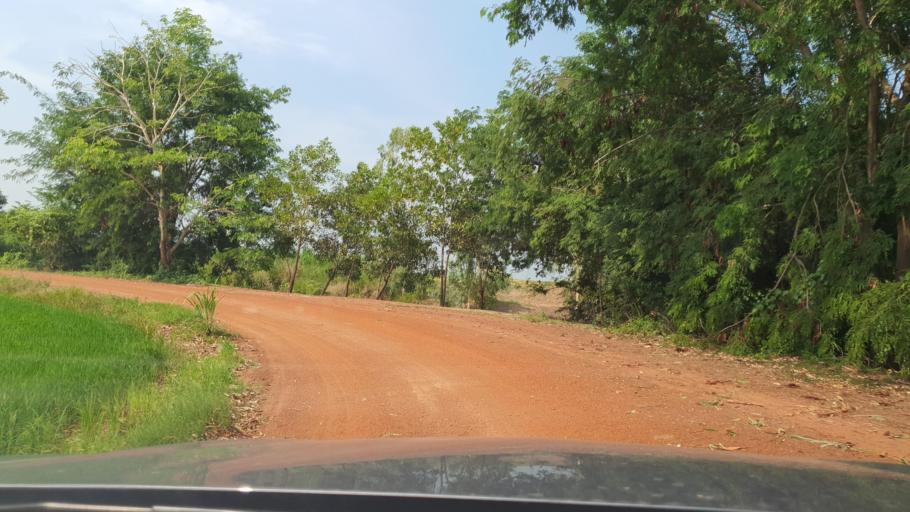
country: TH
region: Phitsanulok
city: Bang Rakam
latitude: 16.7966
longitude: 100.1072
